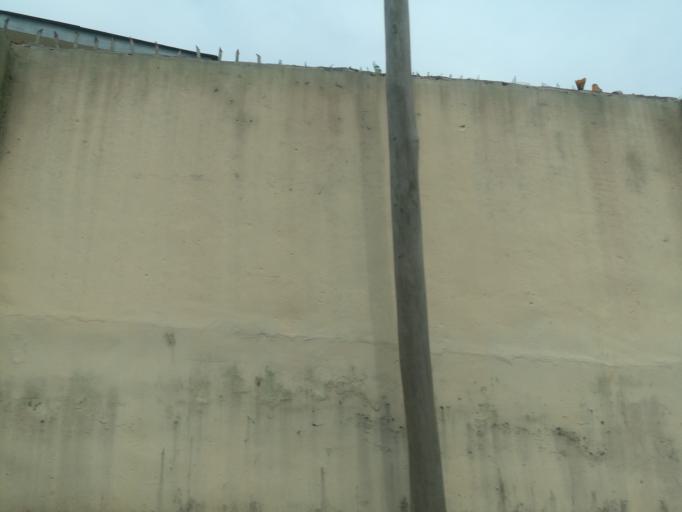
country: NG
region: Oyo
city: Ibadan
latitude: 7.4261
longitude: 3.9209
